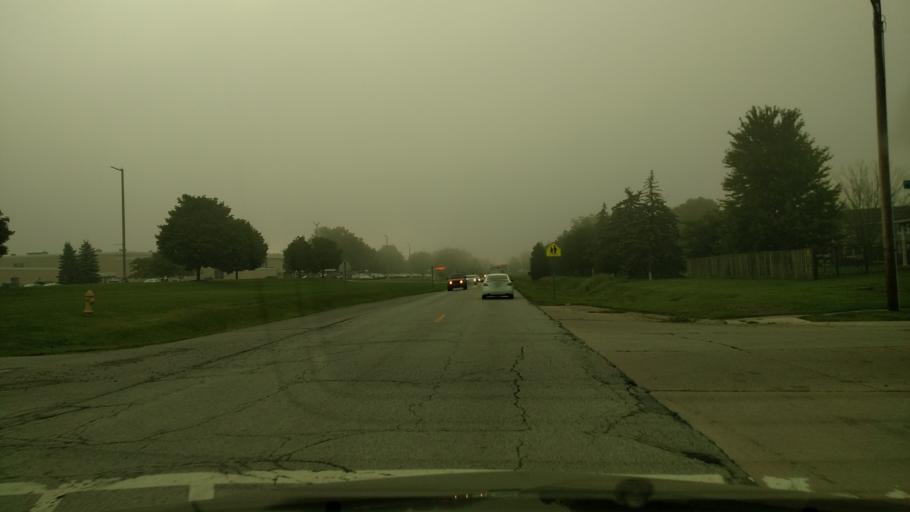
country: US
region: Indiana
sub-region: Howard County
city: Kokomo
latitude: 40.4546
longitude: -86.1604
